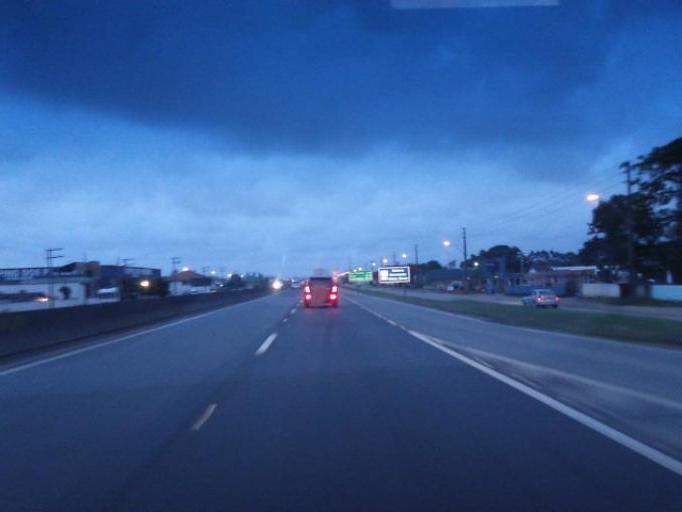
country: BR
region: Santa Catarina
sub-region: Barra Velha
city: Barra Velha
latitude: -26.6535
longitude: -48.6875
